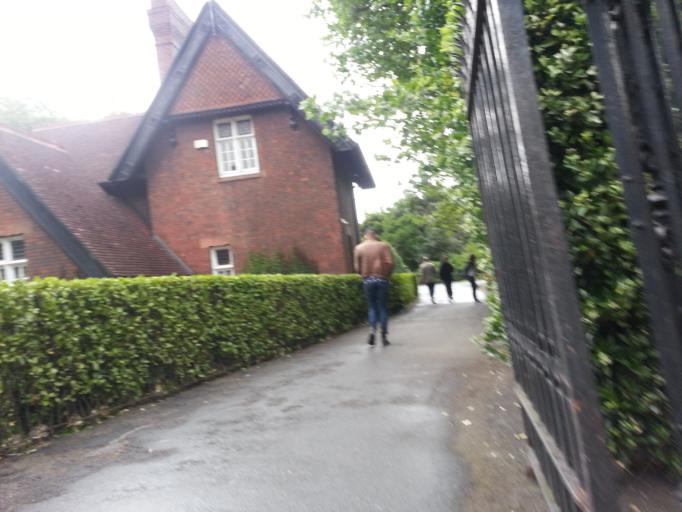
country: IE
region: Leinster
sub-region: Dublin City
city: Dublin
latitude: 53.3376
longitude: -6.2622
